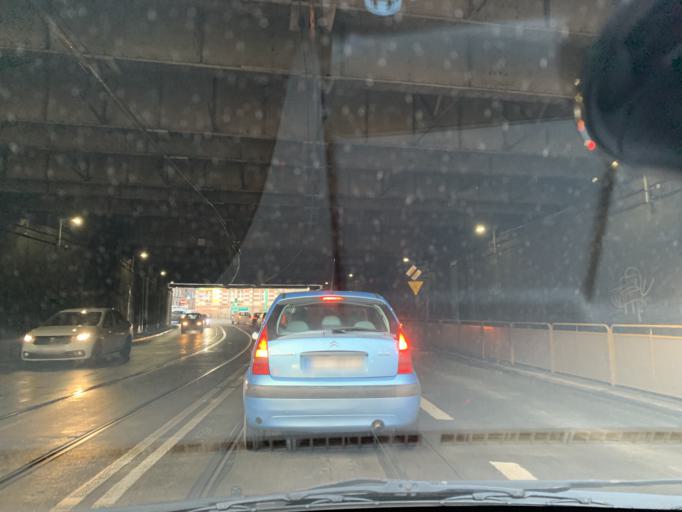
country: PL
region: Silesian Voivodeship
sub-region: Bytom
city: Bytom
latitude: 50.3423
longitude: 18.9171
